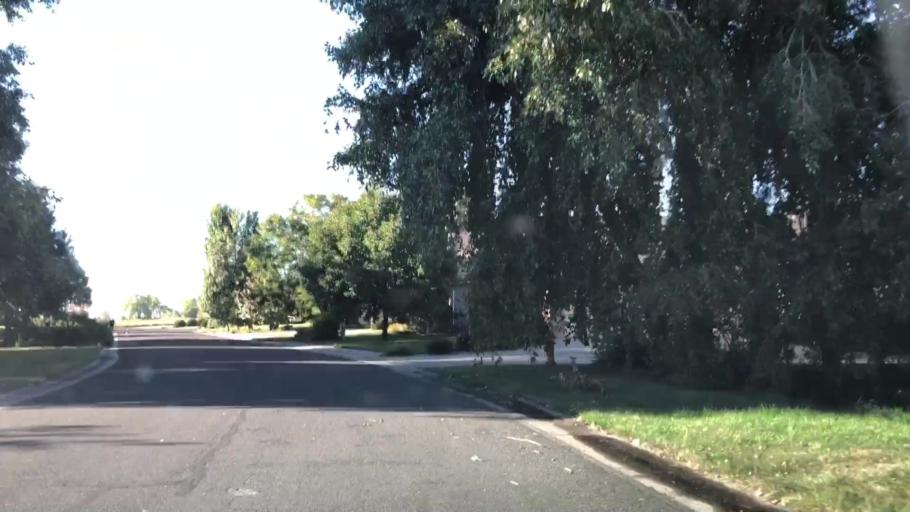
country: US
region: Colorado
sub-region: Larimer County
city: Campion
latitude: 40.3760
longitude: -105.1511
